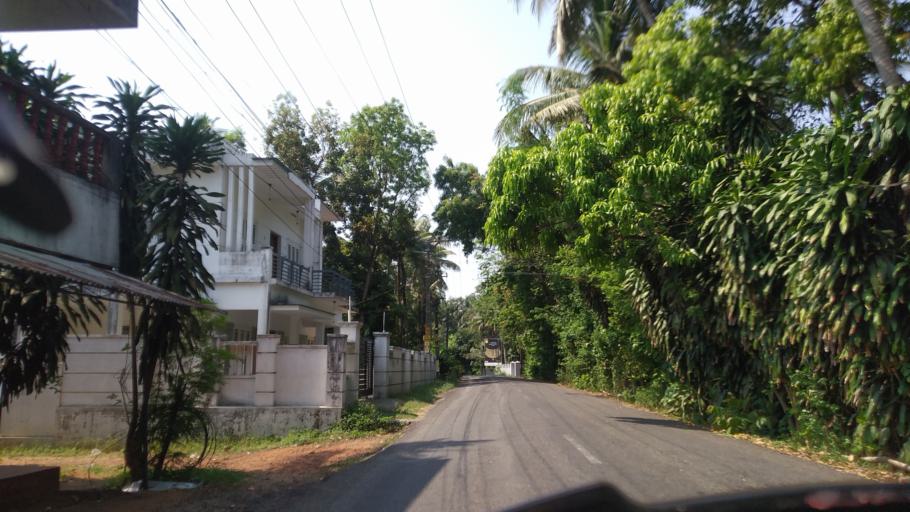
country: IN
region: Kerala
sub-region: Thrissur District
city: Irinjalakuda
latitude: 10.2946
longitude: 76.1332
